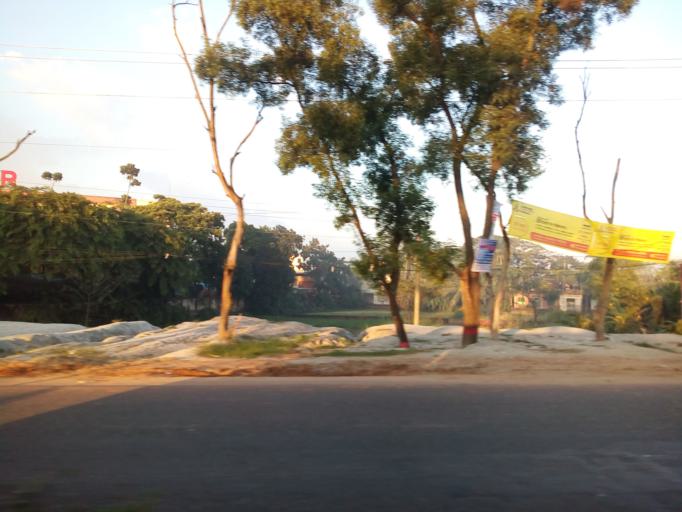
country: BD
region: Dhaka
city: Azimpur
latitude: 23.8022
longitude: 90.2624
